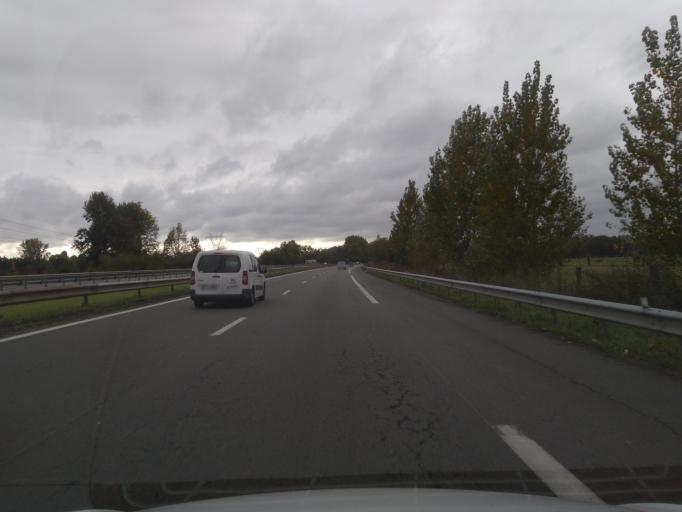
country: FR
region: Nord-Pas-de-Calais
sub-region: Departement du Nord
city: Genech
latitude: 50.5398
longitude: 3.1965
